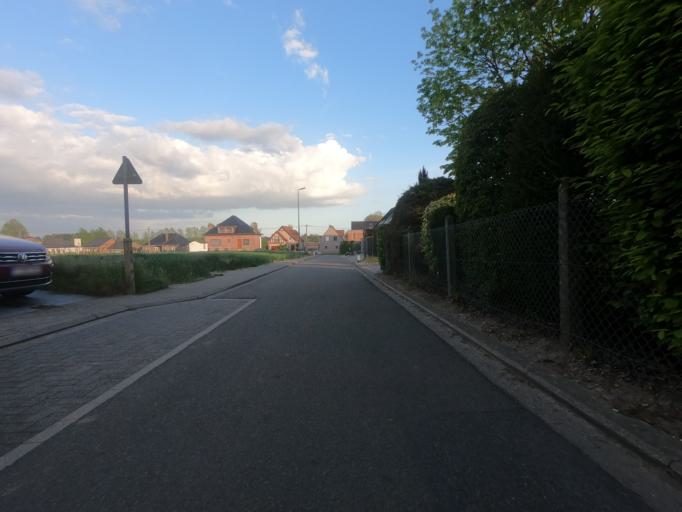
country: BE
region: Flanders
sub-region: Provincie Vlaams-Brabant
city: Gooik
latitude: 50.7789
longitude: 4.1245
